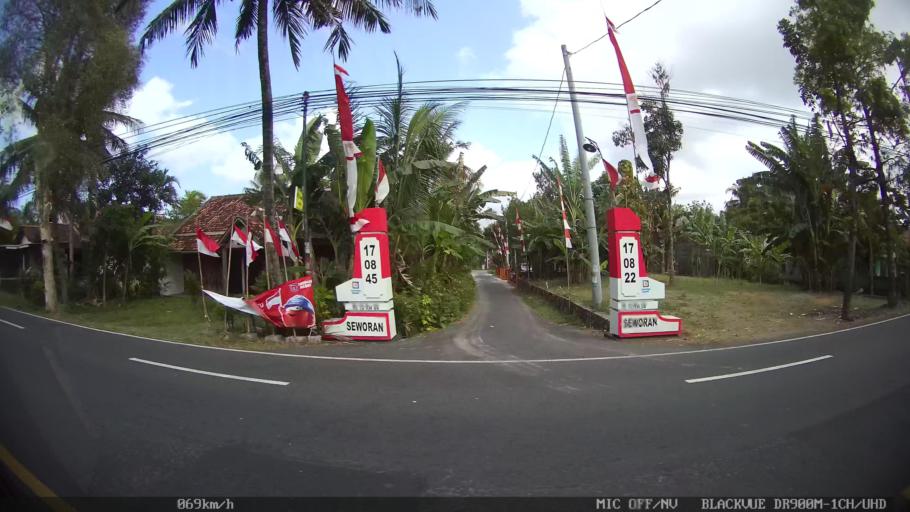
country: ID
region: Daerah Istimewa Yogyakarta
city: Srandakan
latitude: -7.8883
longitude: 110.1301
